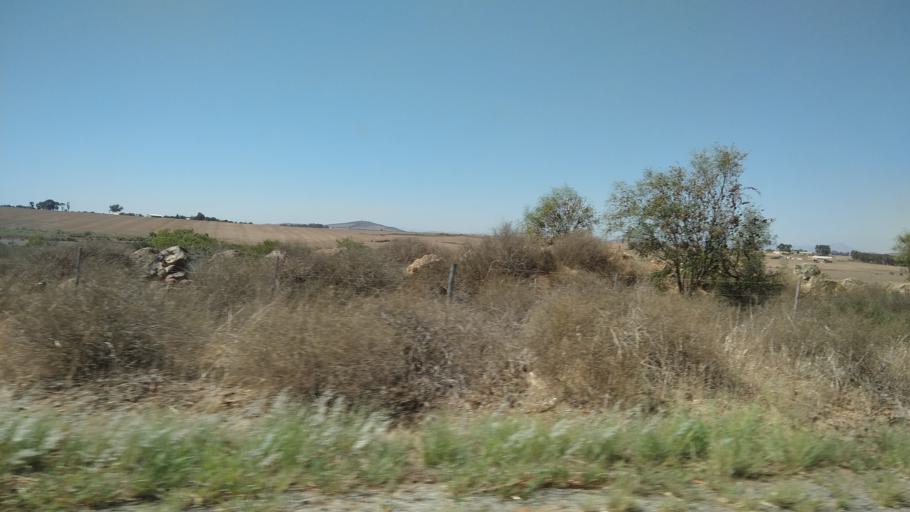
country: ZA
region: Western Cape
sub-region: West Coast District Municipality
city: Moorreesburg
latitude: -33.2484
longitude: 18.5798
